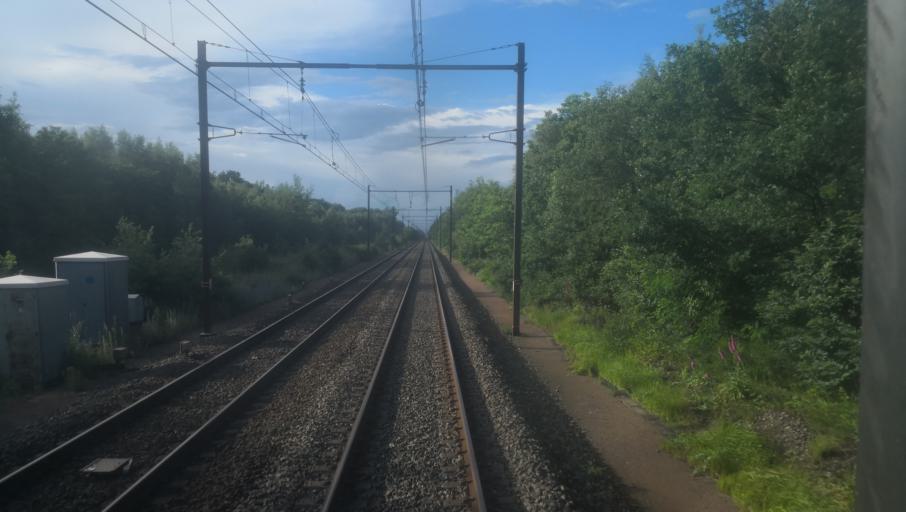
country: FR
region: Centre
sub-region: Departement du Loir-et-Cher
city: Salbris
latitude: 47.4692
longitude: 2.0403
